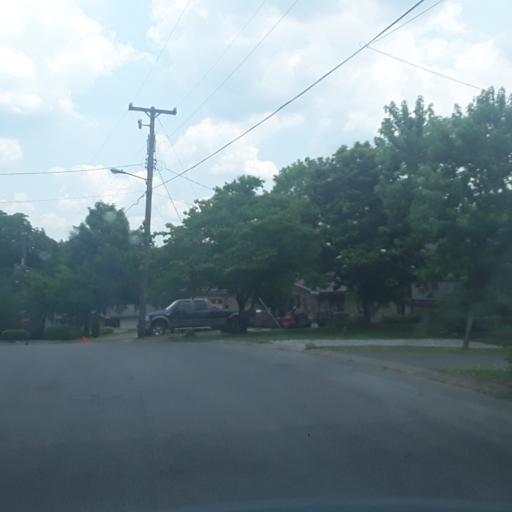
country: US
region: Tennessee
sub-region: Williamson County
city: Brentwood Estates
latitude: 36.0558
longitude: -86.6952
